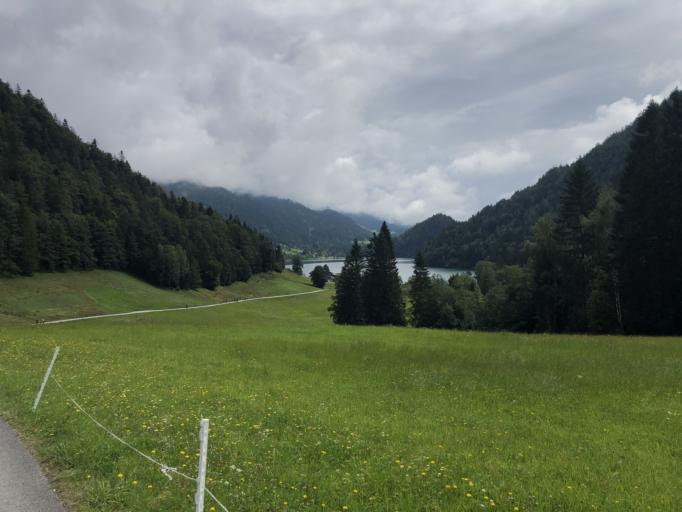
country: AT
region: Tyrol
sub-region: Politischer Bezirk Kufstein
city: Soll
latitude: 47.5397
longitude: 12.1973
